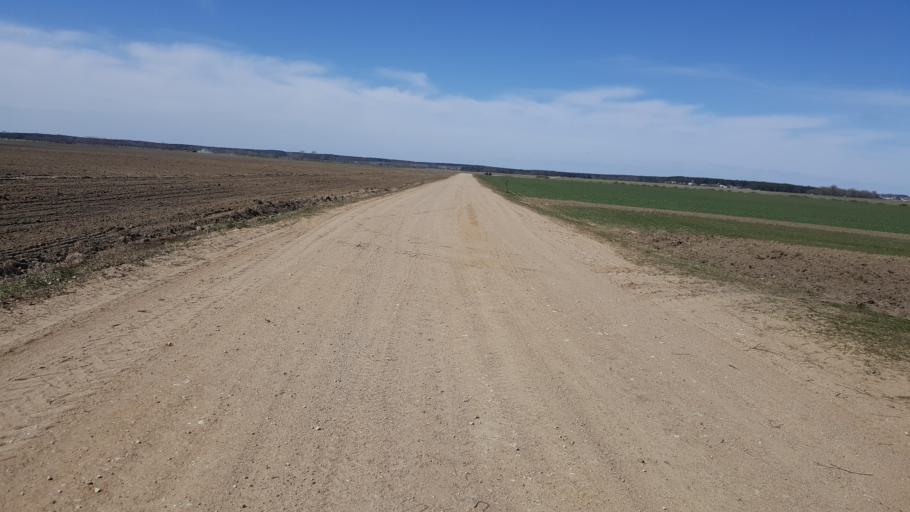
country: BY
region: Brest
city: Zhabinka
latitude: 52.2975
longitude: 23.9121
